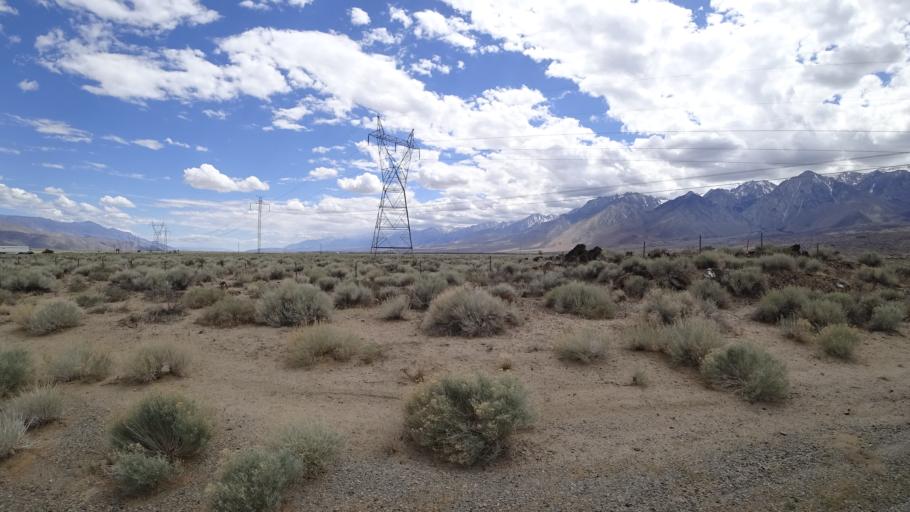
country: US
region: California
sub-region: Inyo County
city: Big Pine
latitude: 36.9787
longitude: -118.2384
